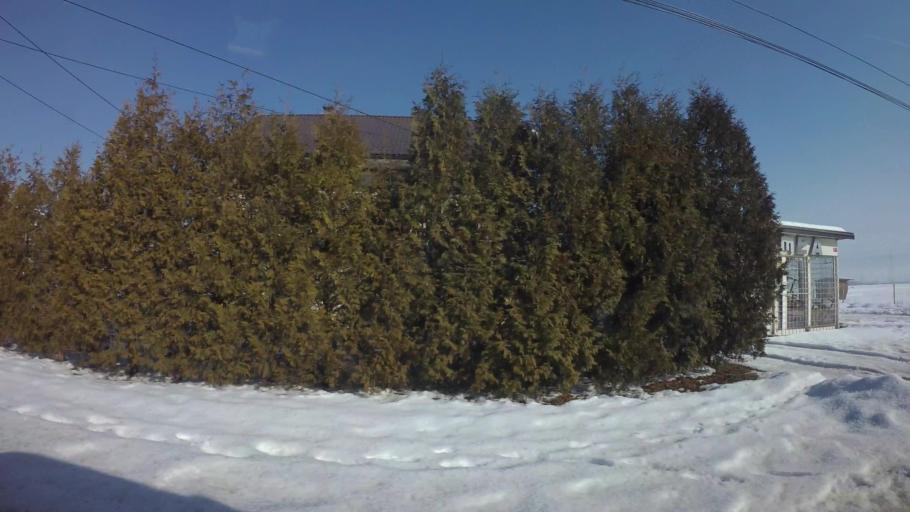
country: BA
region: Federation of Bosnia and Herzegovina
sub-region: Kanton Sarajevo
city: Sarajevo
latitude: 43.8048
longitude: 18.3030
